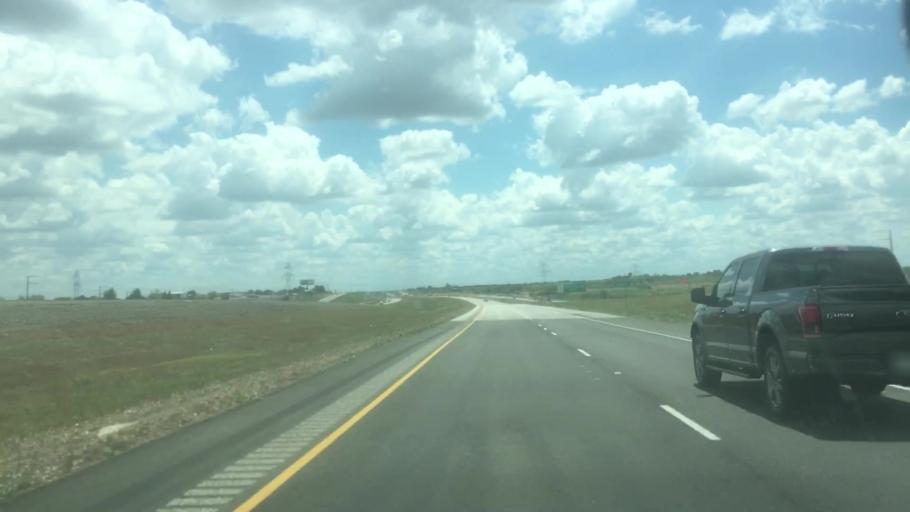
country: US
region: Texas
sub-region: Caldwell County
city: Uhland
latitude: 30.0031
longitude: -97.6874
